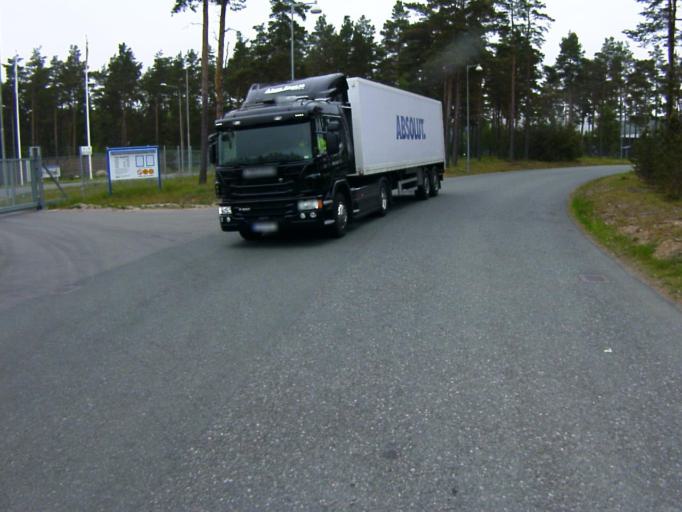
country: SE
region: Skane
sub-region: Kristianstads Kommun
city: Ahus
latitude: 55.9296
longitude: 14.2740
